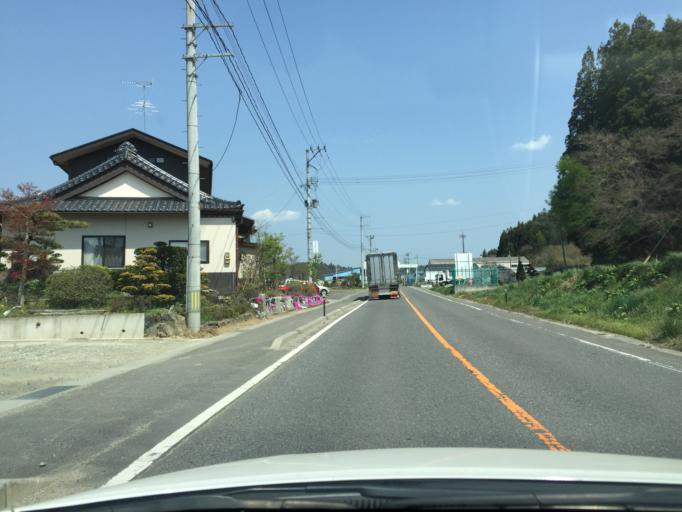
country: JP
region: Fukushima
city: Funehikimachi-funehiki
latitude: 37.4410
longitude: 140.5995
